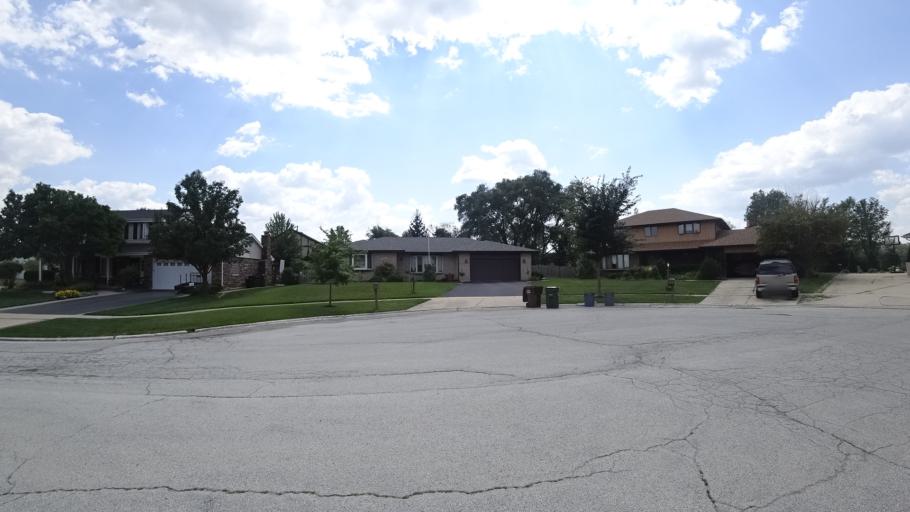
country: US
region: Illinois
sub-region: Cook County
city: Oak Forest
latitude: 41.6187
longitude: -87.7755
